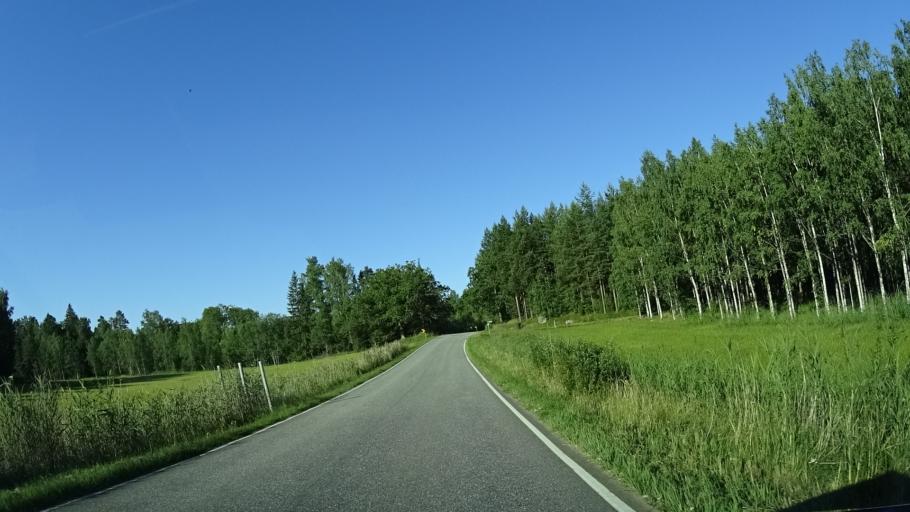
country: FI
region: Varsinais-Suomi
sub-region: Turku
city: Merimasku
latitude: 60.4990
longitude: 21.7901
